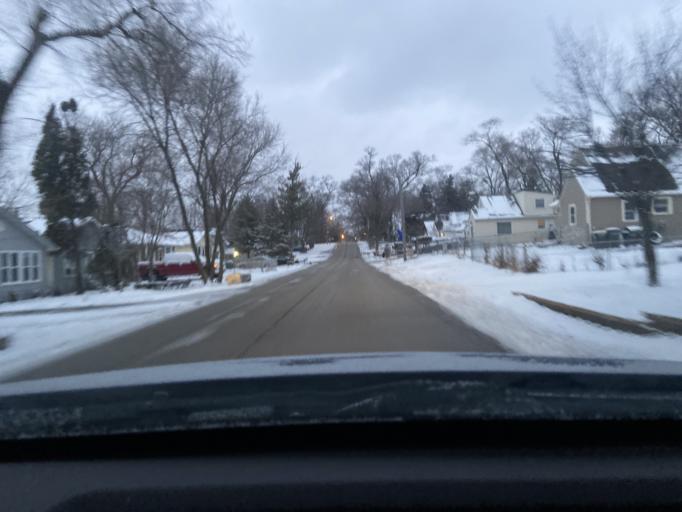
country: US
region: Illinois
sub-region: Lake County
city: Round Lake Park
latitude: 42.3538
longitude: -88.0797
